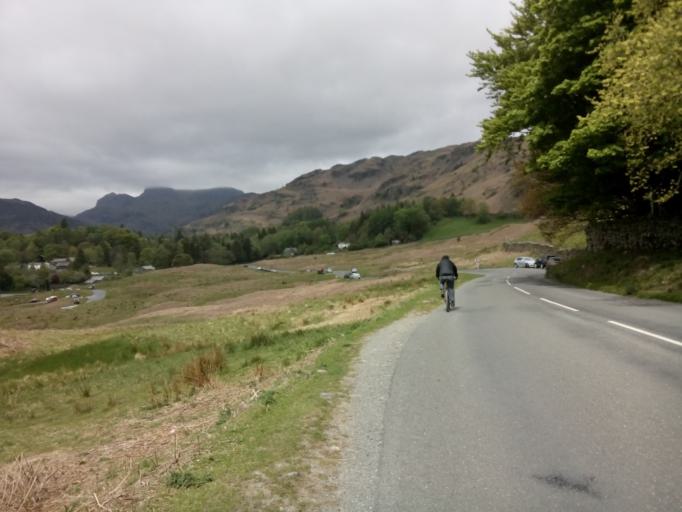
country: GB
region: England
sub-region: Cumbria
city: Ambleside
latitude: 54.4338
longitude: -3.0297
